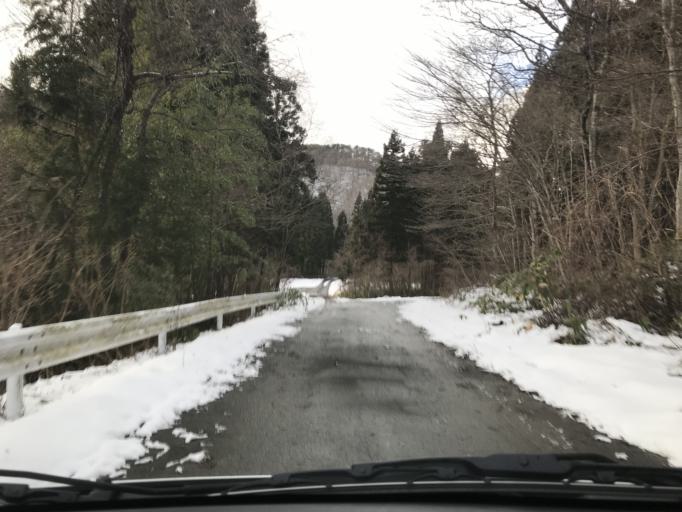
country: JP
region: Iwate
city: Ichinoseki
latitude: 39.0192
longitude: 140.9689
